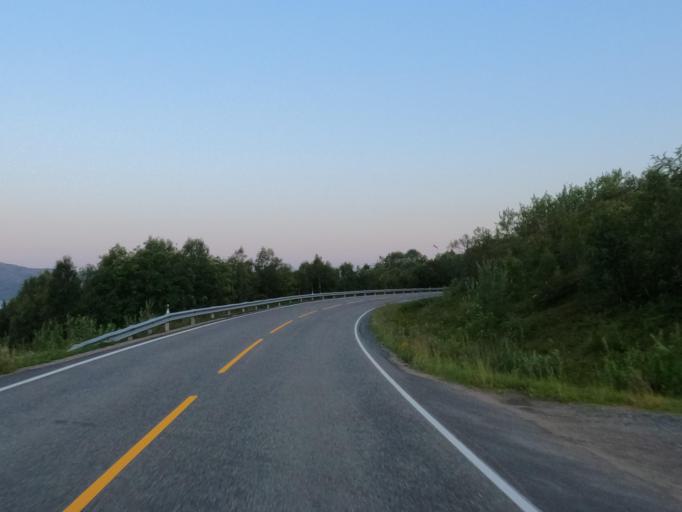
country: NO
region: Nordland
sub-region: Lodingen
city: Lodingen
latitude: 68.5162
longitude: 16.1044
